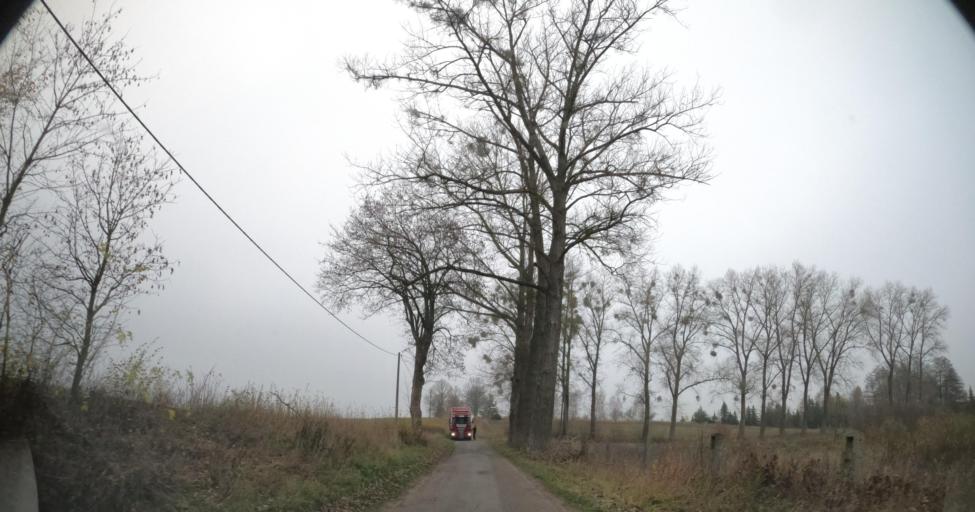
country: PL
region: West Pomeranian Voivodeship
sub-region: Powiat drawski
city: Drawsko Pomorskie
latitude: 53.5718
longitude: 15.8340
